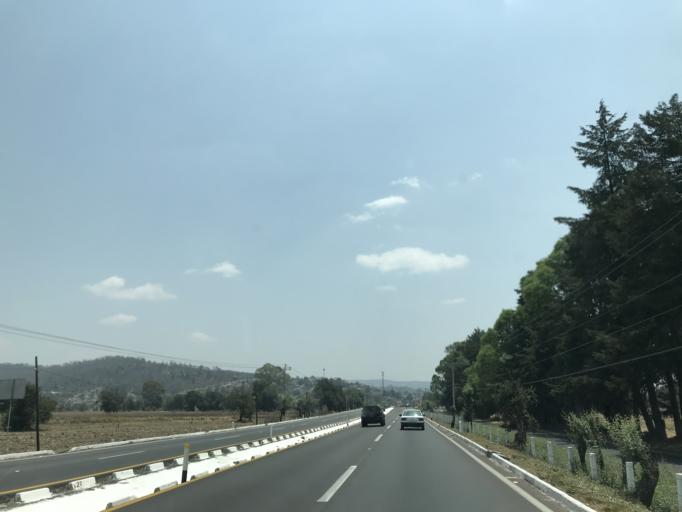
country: MX
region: Tlaxcala
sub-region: Ixtacuixtla de Mariano Matamoros
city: Santa Justina Ecatepec
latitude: 19.3284
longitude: -98.3594
